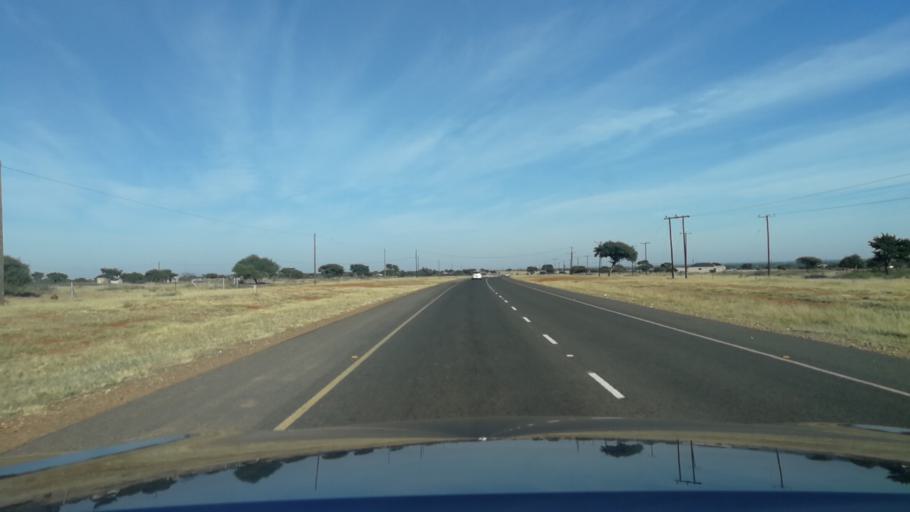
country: BW
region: South East
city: Janeng
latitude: -25.4721
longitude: 25.5300
